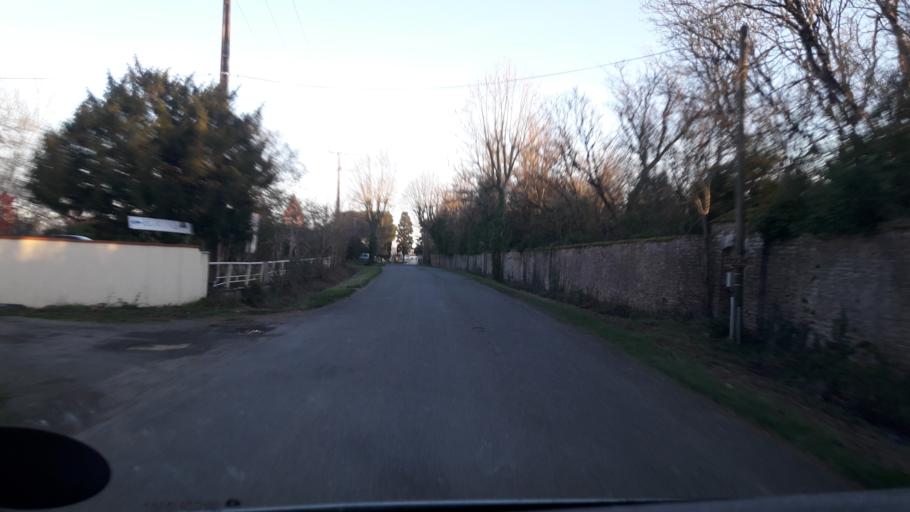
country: FR
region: Midi-Pyrenees
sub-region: Departement du Gers
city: Gimont
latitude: 43.6013
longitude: 0.9799
